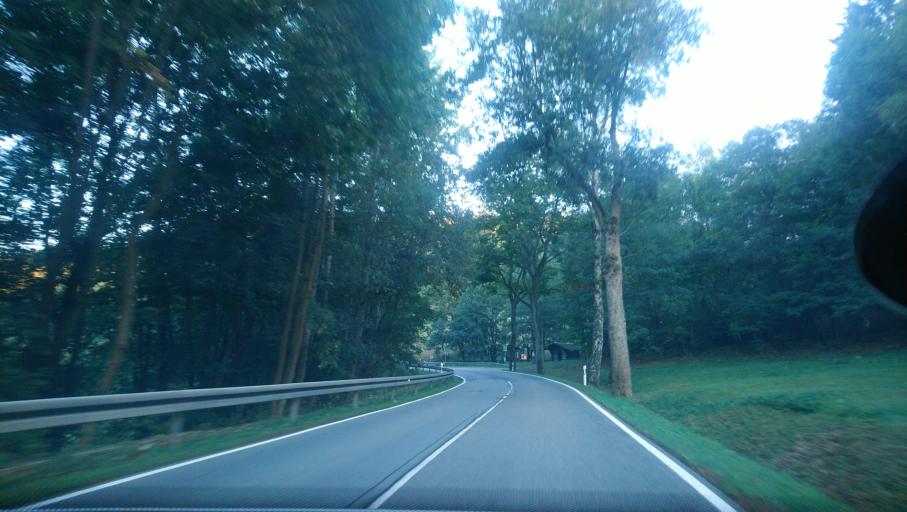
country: DE
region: Saxony
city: Tannenberg
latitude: 50.6035
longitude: 12.9796
